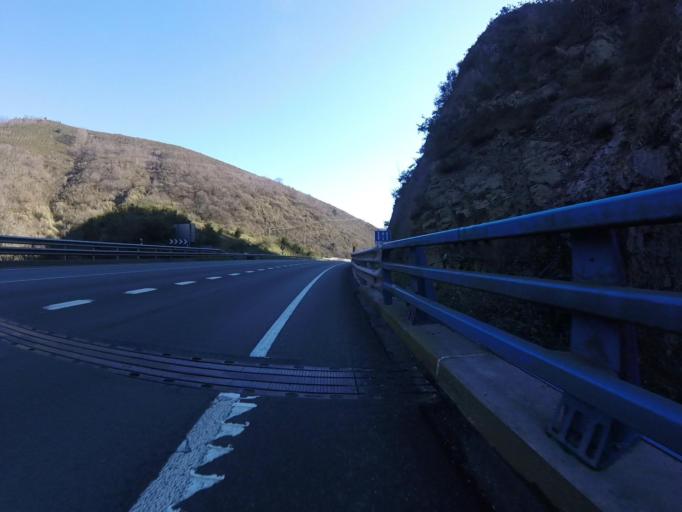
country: ES
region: Navarre
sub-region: Provincia de Navarra
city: Bera
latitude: 43.2901
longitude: -1.7128
